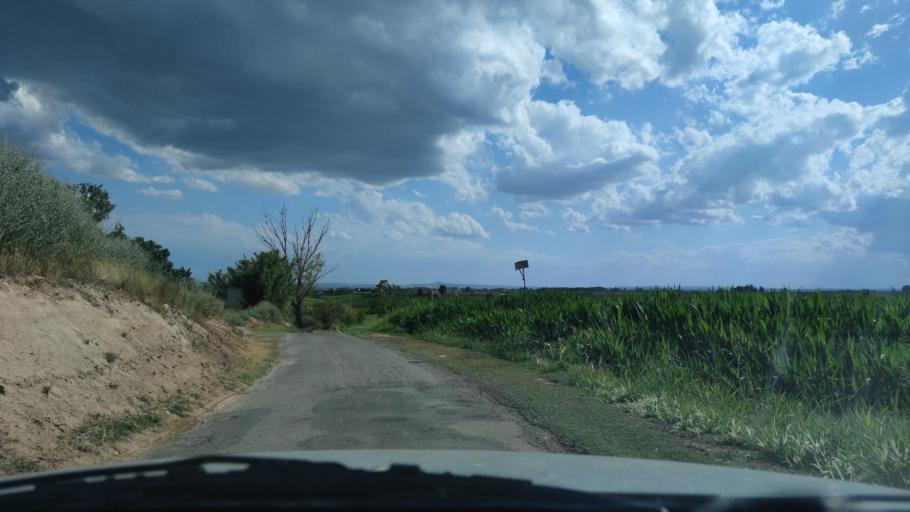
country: ES
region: Catalonia
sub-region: Provincia de Lleida
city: Alcarras
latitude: 41.5902
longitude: 0.5392
